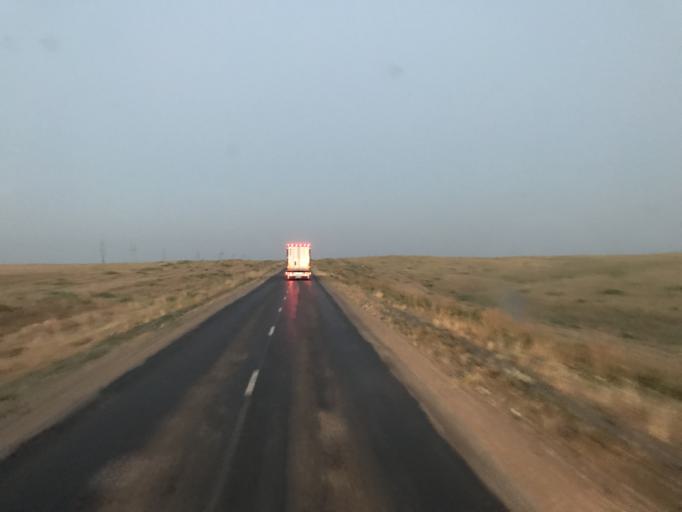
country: UZ
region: Toshkent
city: Chinoz
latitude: 41.1486
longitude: 68.6856
